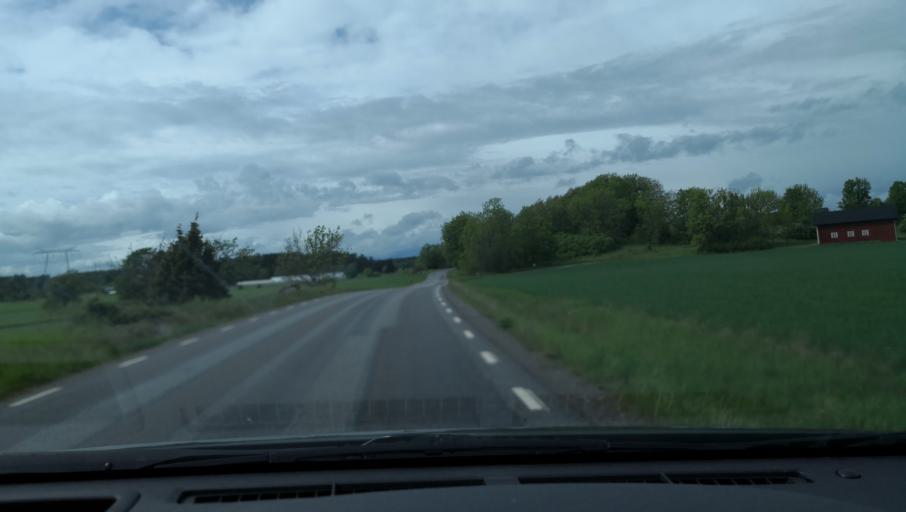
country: SE
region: Uppsala
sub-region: Enkopings Kommun
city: Orsundsbro
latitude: 59.6997
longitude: 17.3645
